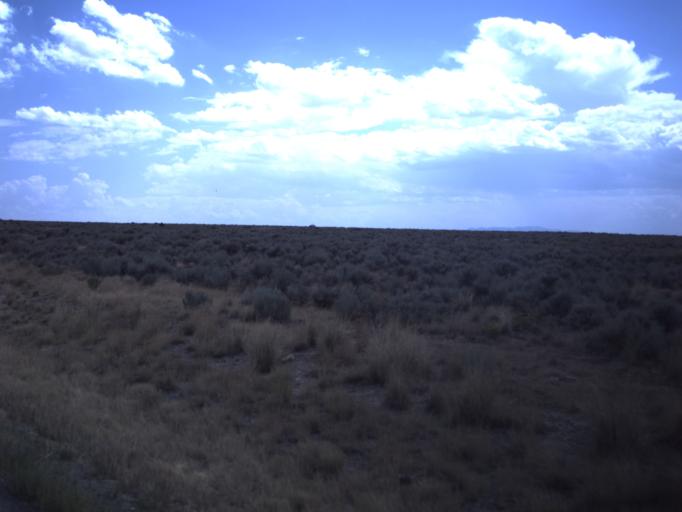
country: US
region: Utah
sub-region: Tooele County
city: Tooele
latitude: 40.3639
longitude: -112.3377
